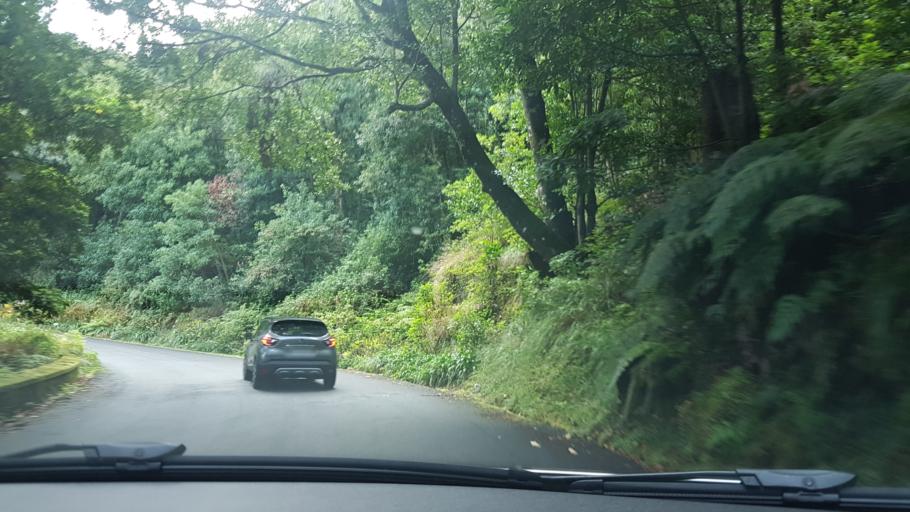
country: PT
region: Madeira
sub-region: Sao Vicente
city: Sao Vicente
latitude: 32.7634
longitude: -17.0265
